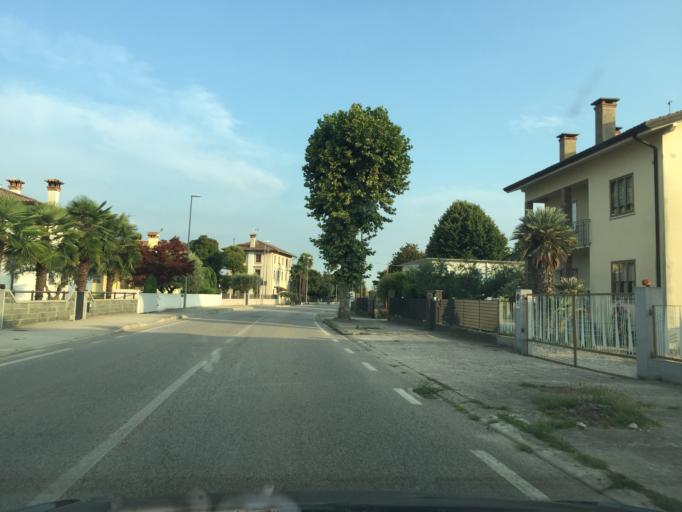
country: IT
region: Friuli Venezia Giulia
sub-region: Provincia di Udine
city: Percoto
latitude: 45.9719
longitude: 13.3301
